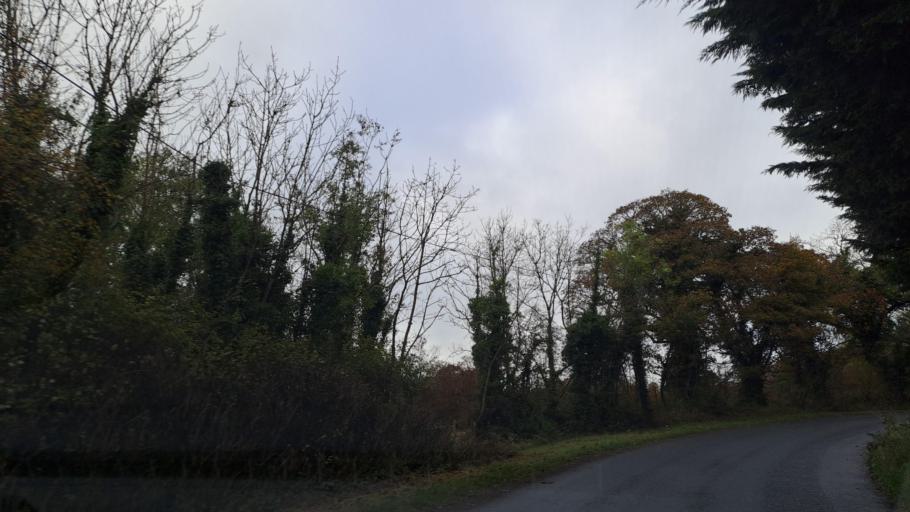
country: IE
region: Ulster
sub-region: An Cabhan
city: Bailieborough
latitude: 53.9907
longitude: -6.9889
